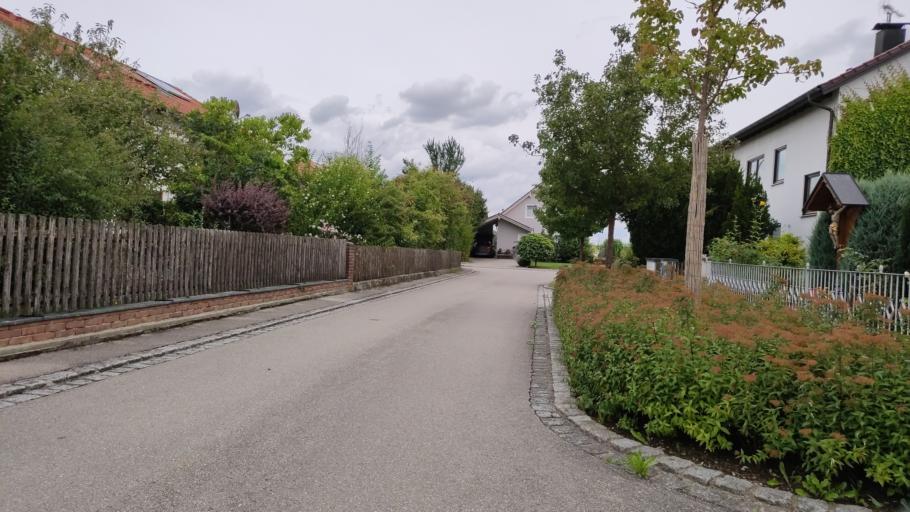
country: DE
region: Bavaria
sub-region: Swabia
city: Wehringen
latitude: 48.2419
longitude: 10.8013
